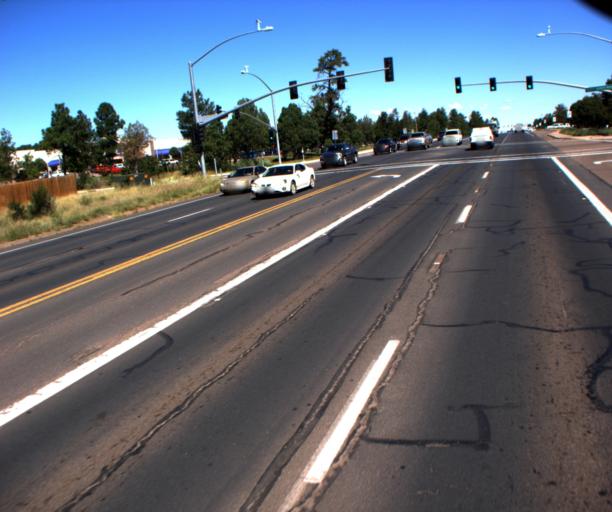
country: US
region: Arizona
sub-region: Navajo County
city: Lake of the Woods
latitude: 34.1962
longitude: -110.0166
